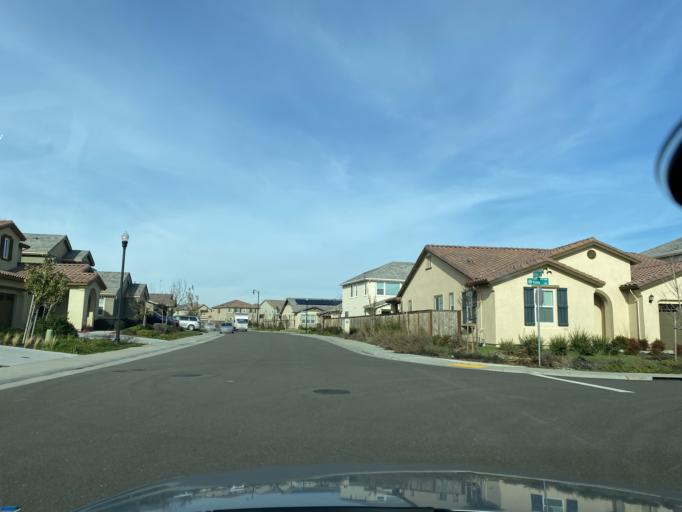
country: US
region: California
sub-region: Sacramento County
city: Elk Grove
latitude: 38.3990
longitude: -121.3863
